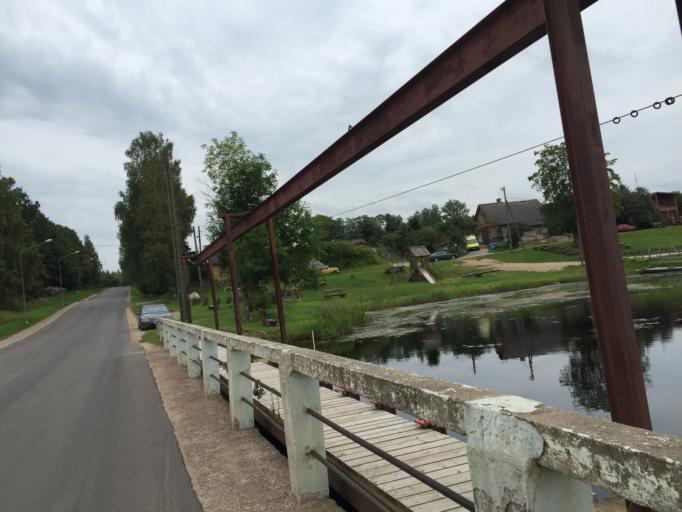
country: LV
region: Zilupes
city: Zilupe
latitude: 56.3903
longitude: 28.1323
